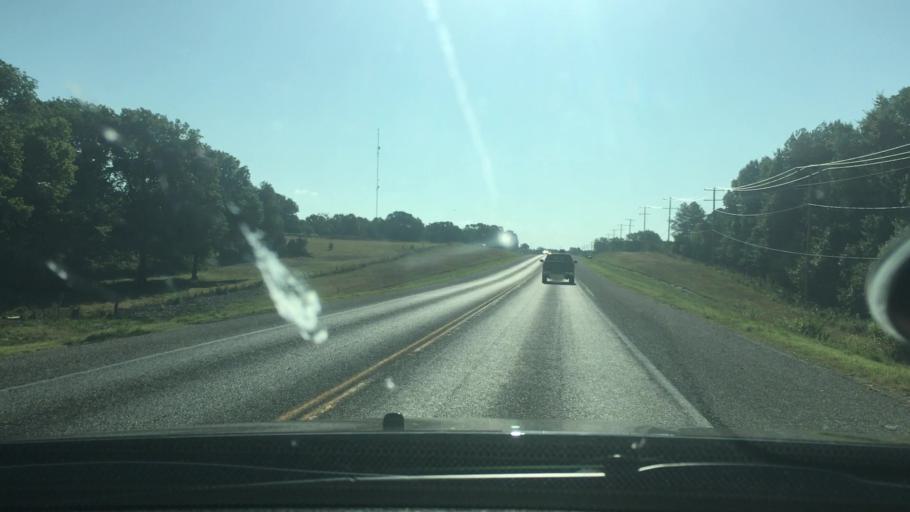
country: US
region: Oklahoma
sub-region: Johnston County
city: Tishomingo
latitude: 34.2369
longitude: -96.7106
